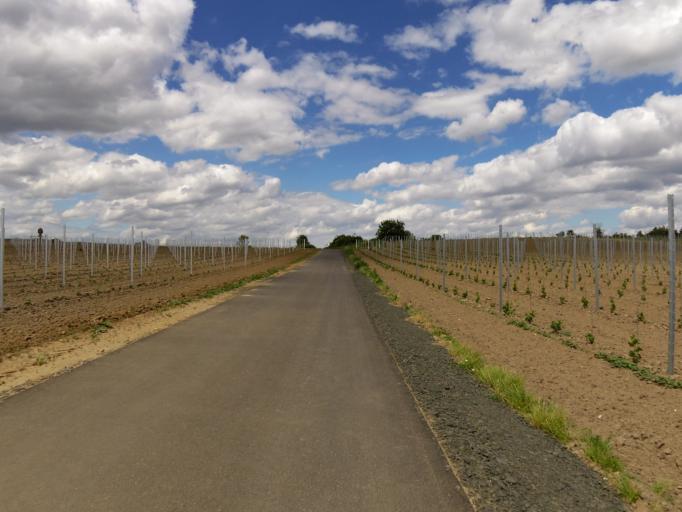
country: DE
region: Rheinland-Pfalz
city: Freinsheim
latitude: 49.4968
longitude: 8.2007
